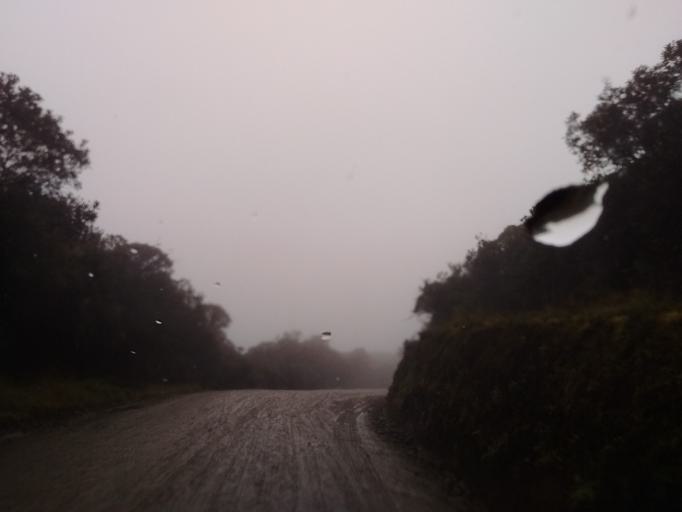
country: CO
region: Cauca
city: Paispamba
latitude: 2.1515
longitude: -76.4238
